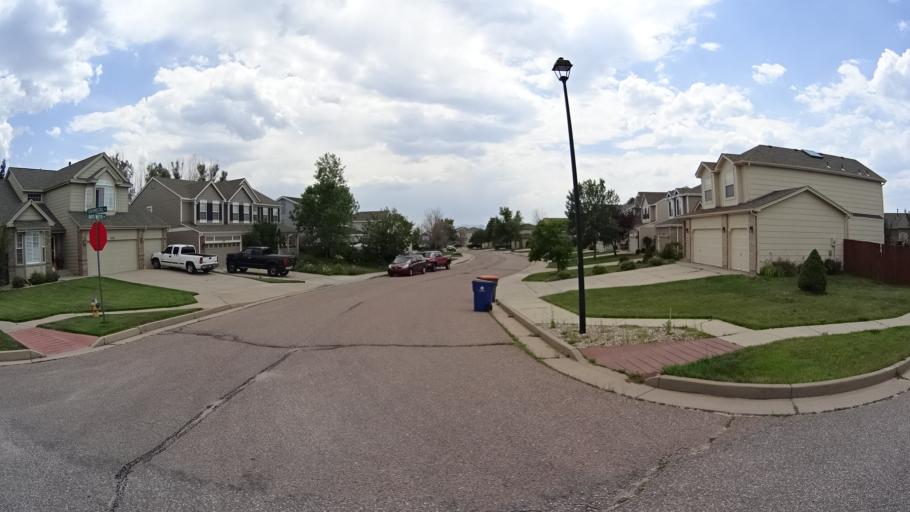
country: US
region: Colorado
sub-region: El Paso County
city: Black Forest
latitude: 38.9637
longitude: -104.7419
